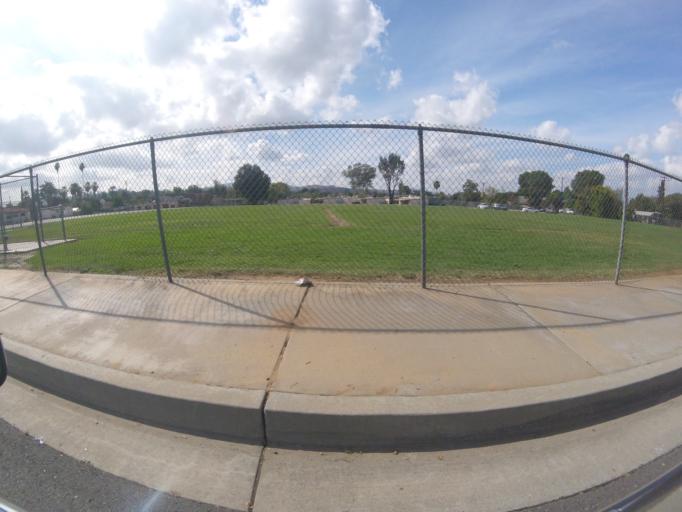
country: US
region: California
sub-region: San Bernardino County
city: Redlands
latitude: 34.0433
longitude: -117.1863
